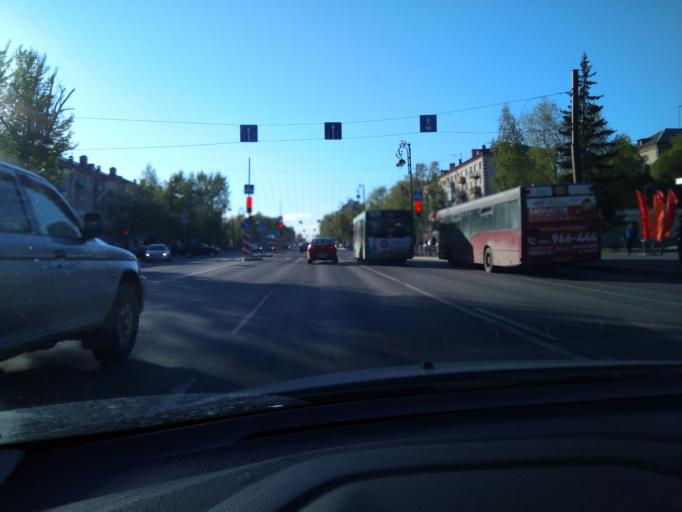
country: RU
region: Tjumen
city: Tyumen
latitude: 57.1337
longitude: 65.5775
